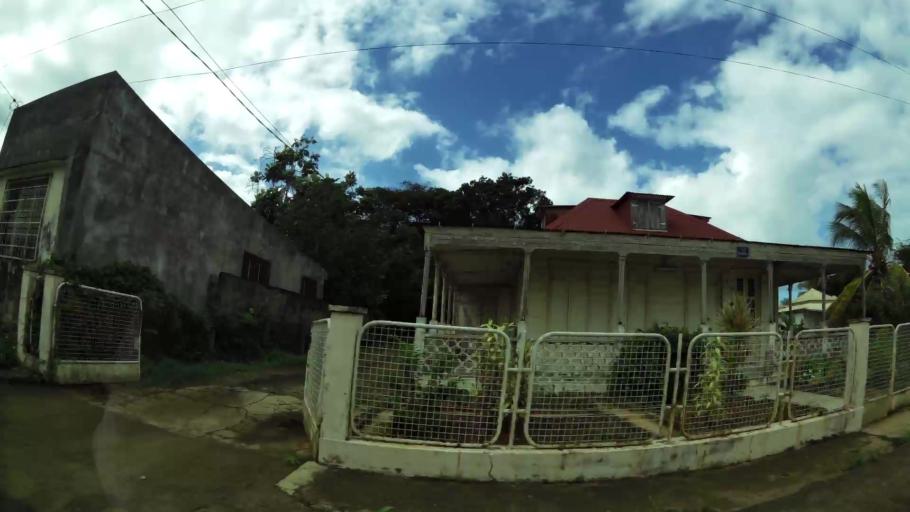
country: GP
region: Guadeloupe
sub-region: Guadeloupe
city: Sainte-Rose
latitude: 16.3261
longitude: -61.7011
